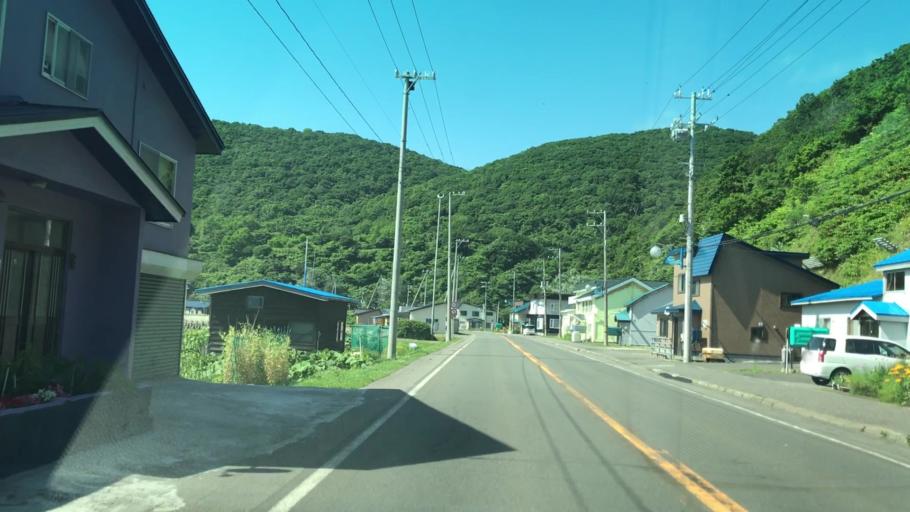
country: JP
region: Hokkaido
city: Iwanai
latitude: 43.1036
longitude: 140.4600
